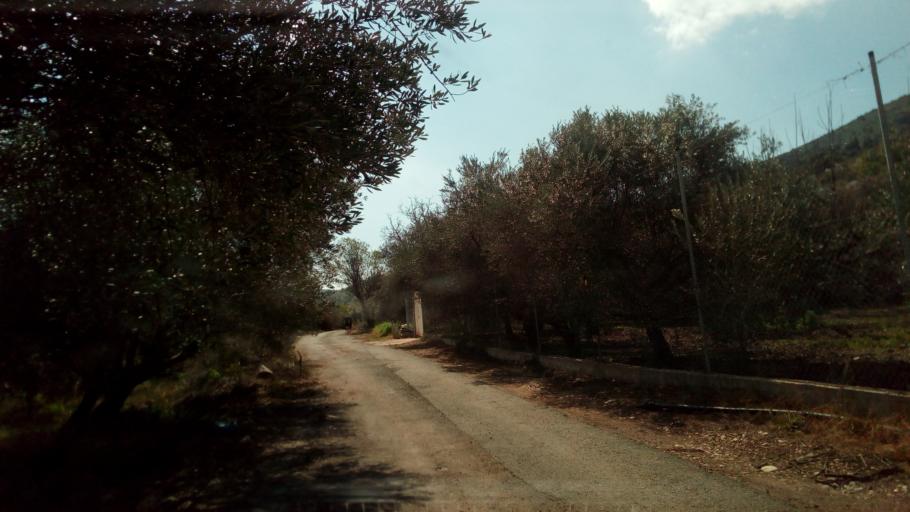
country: CY
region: Pafos
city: Mesogi
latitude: 34.8031
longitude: 32.5299
